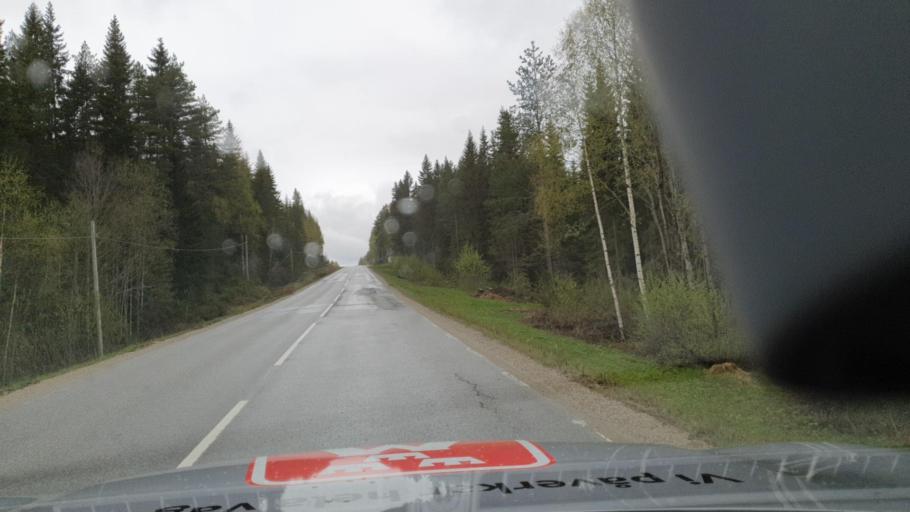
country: SE
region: Vaesternorrland
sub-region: OErnskoeldsviks Kommun
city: Bredbyn
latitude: 63.5103
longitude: 17.7704
